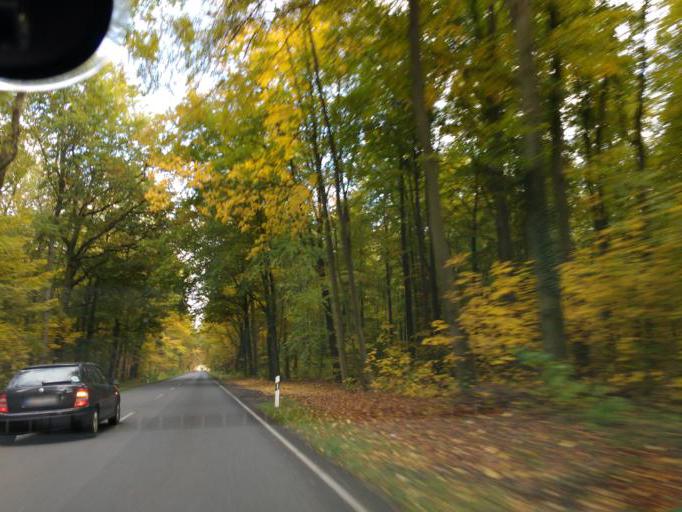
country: DE
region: Brandenburg
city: Petershagen
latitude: 52.5585
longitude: 13.7792
